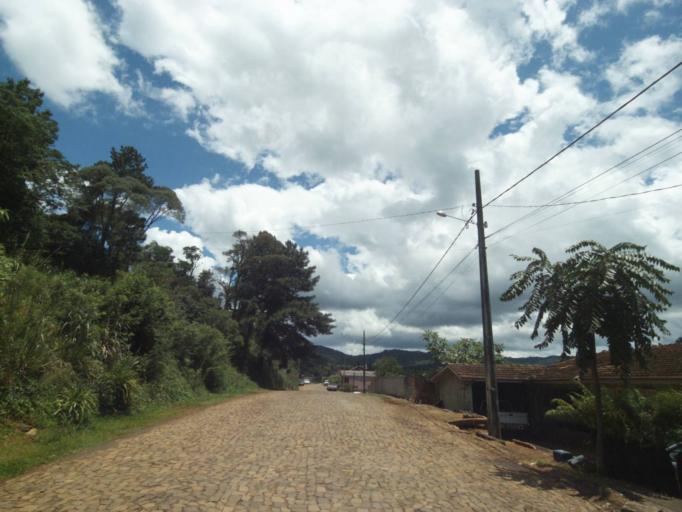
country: BR
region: Parana
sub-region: Uniao Da Vitoria
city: Uniao da Vitoria
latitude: -26.1579
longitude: -51.5519
